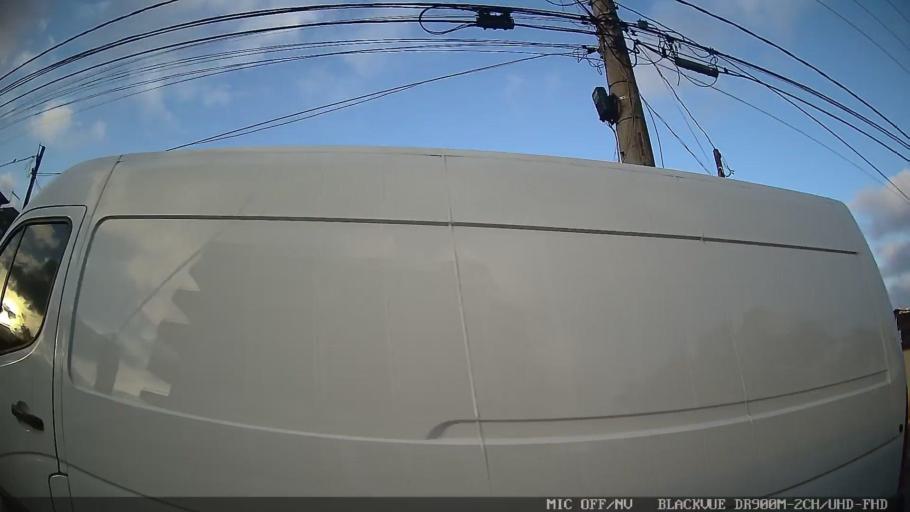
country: BR
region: Sao Paulo
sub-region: Peruibe
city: Peruibe
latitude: -24.3179
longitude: -46.9981
